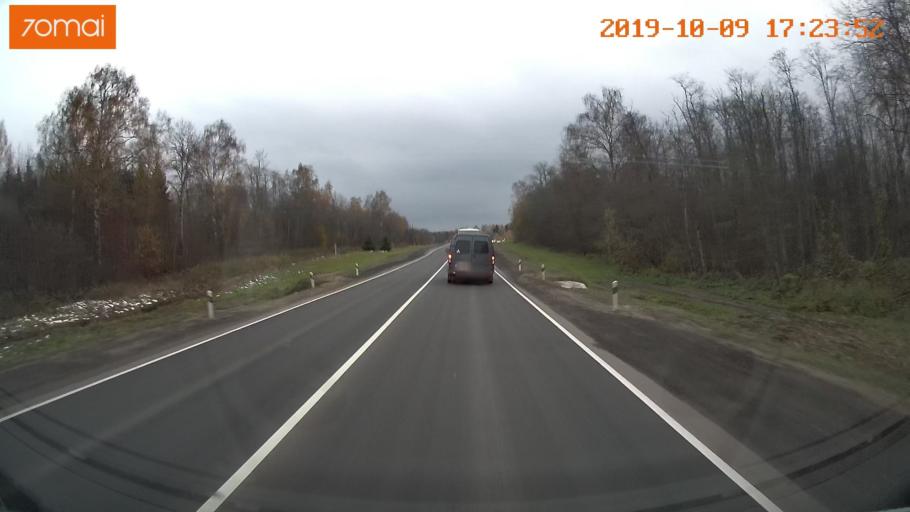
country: RU
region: Ivanovo
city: Furmanov
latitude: 57.1906
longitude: 41.1131
